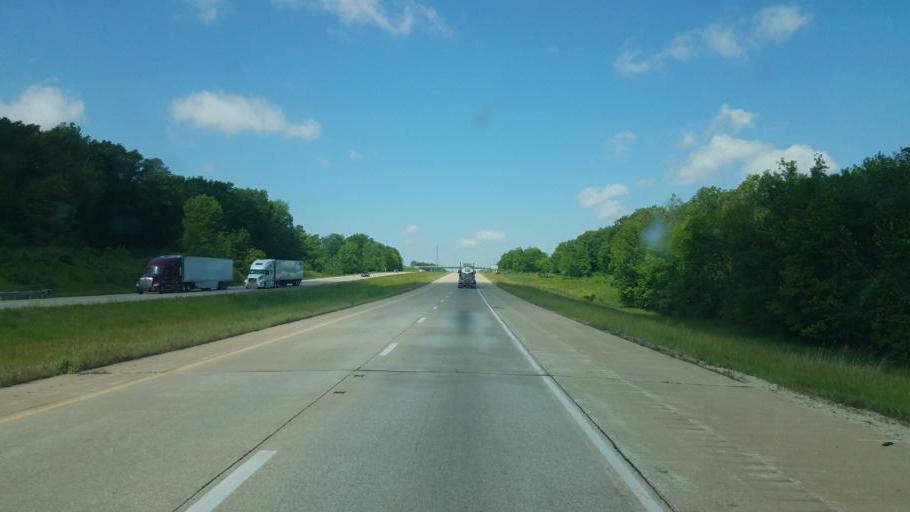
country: US
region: Illinois
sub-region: Clark County
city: Marshall
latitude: 39.4258
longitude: -87.5928
